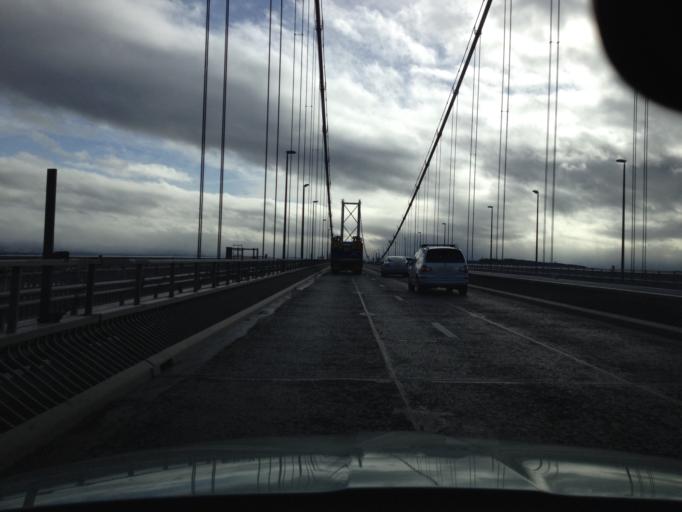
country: GB
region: Scotland
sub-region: Fife
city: North Queensferry
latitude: 56.0051
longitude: -3.4039
